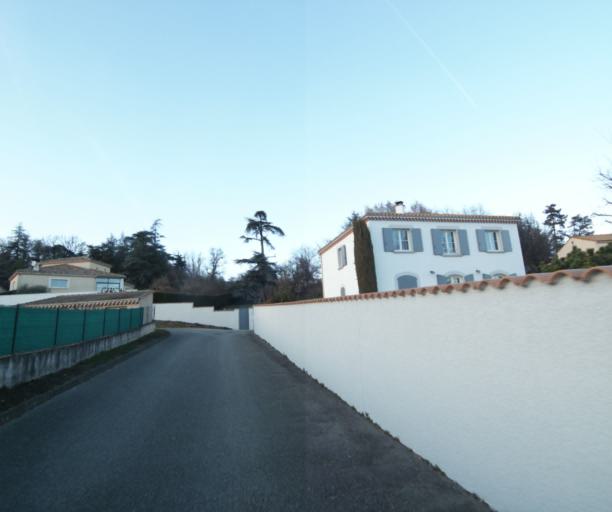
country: FR
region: Rhone-Alpes
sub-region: Departement de l'Ardeche
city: Davezieux
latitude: 45.2488
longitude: 4.7113
